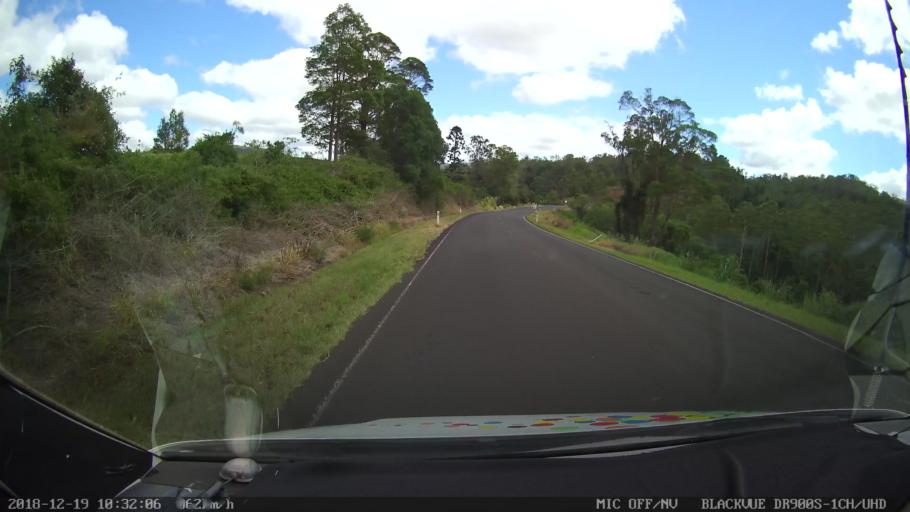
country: AU
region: New South Wales
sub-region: Lismore Municipality
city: Larnook
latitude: -28.5847
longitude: 153.1202
